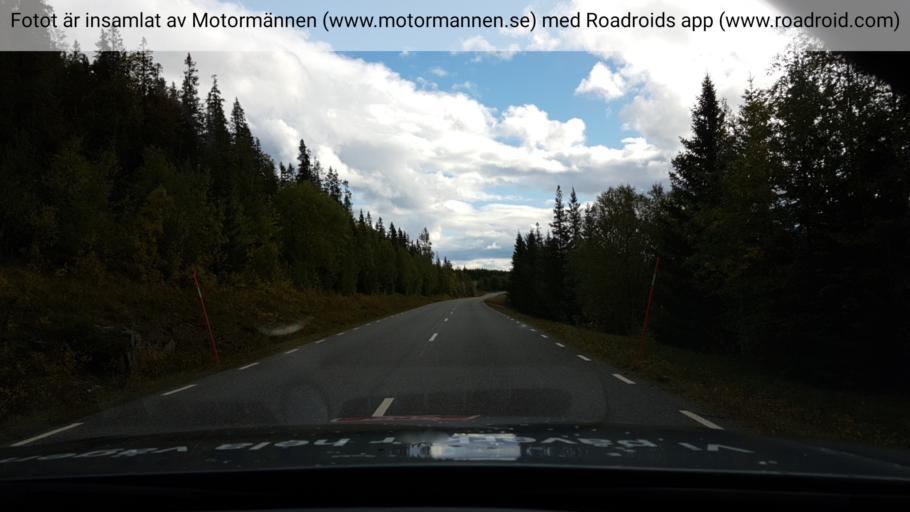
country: SE
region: Jaemtland
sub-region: Are Kommun
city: Are
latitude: 63.5519
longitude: 13.0344
